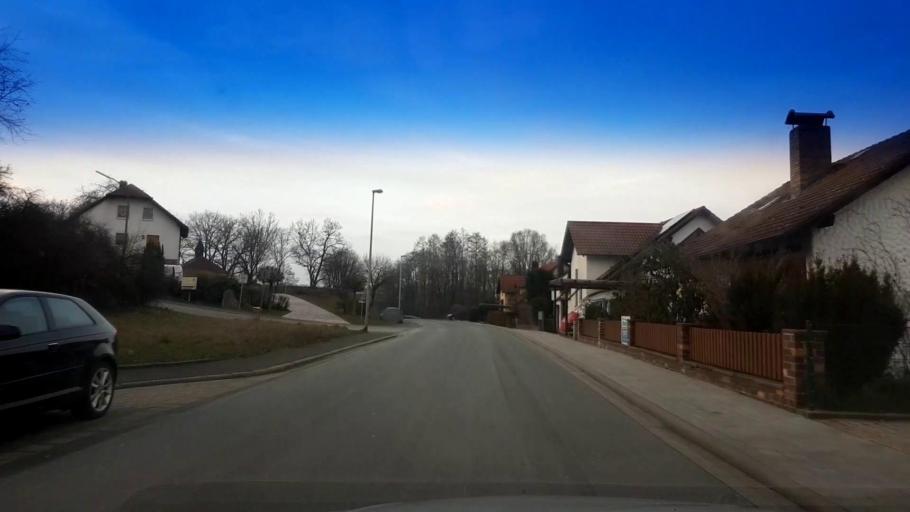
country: DE
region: Bavaria
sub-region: Upper Franconia
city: Altendorf
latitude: 49.7952
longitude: 10.9961
